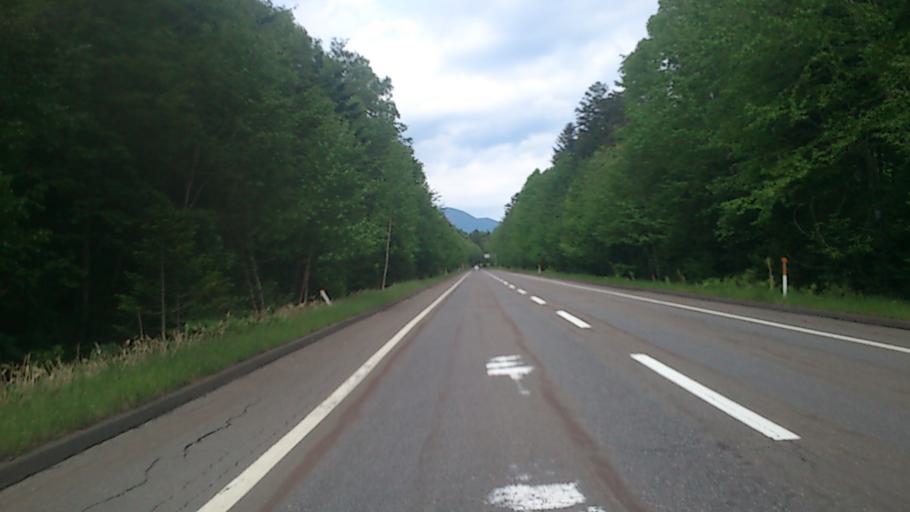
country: JP
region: Hokkaido
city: Kitami
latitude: 43.4055
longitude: 143.9415
